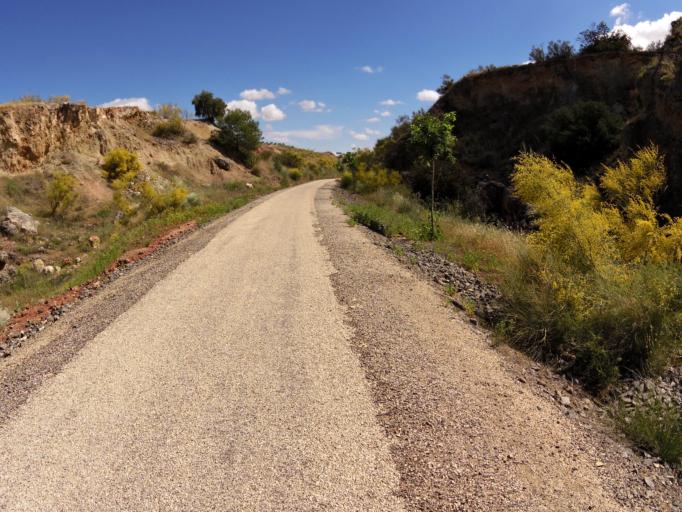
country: ES
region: Andalusia
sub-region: Provincia de Jaen
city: Alcaudete
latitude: 37.6176
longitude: -4.1089
